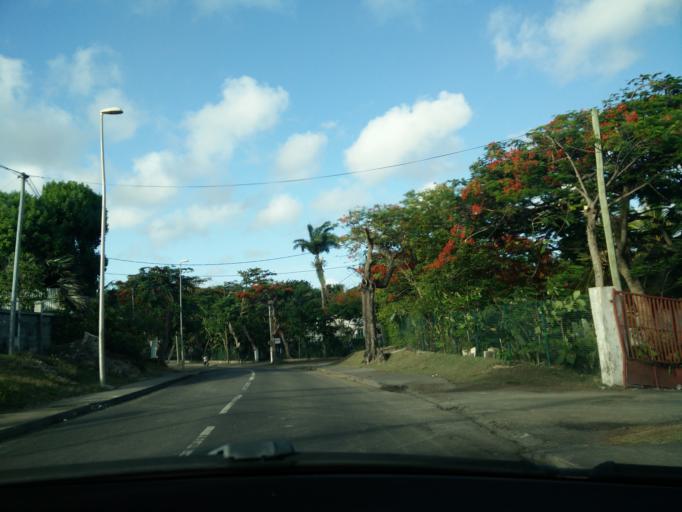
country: GP
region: Guadeloupe
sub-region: Guadeloupe
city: Le Moule
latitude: 16.3257
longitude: -61.3441
